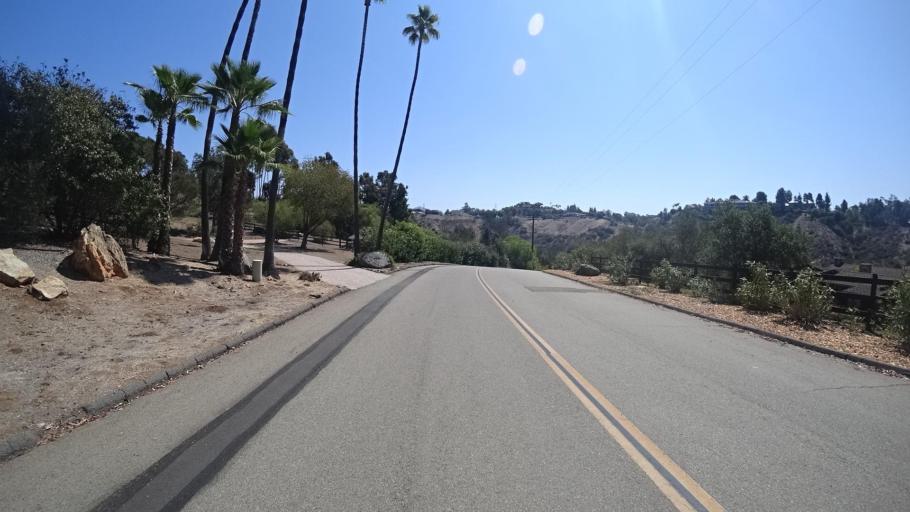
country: US
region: California
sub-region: San Diego County
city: Fairbanks Ranch
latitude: 33.0136
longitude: -117.1783
